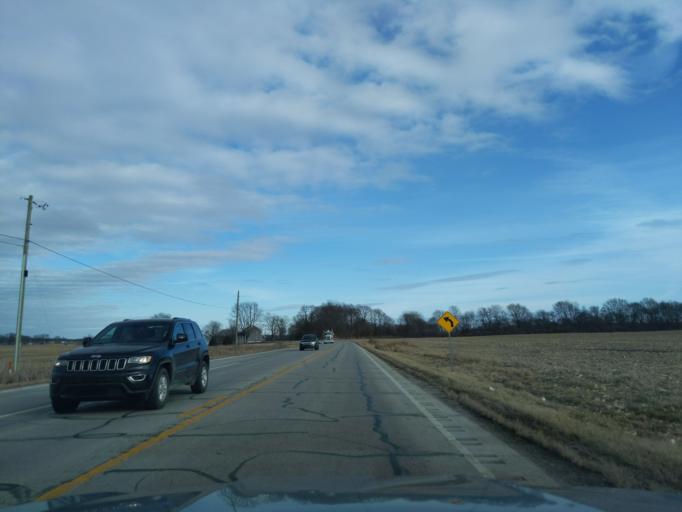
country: US
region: Indiana
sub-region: Tippecanoe County
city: Shadeland
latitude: 40.3594
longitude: -86.9752
